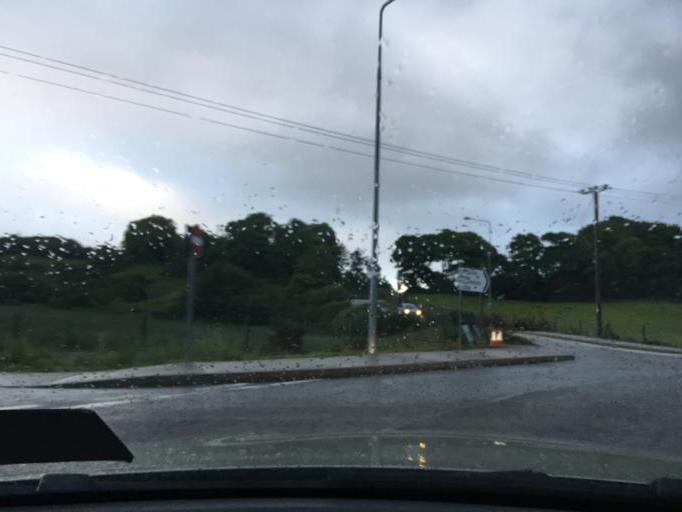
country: IE
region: Ulster
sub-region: County Donegal
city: Killybegs
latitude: 54.6348
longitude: -8.4607
